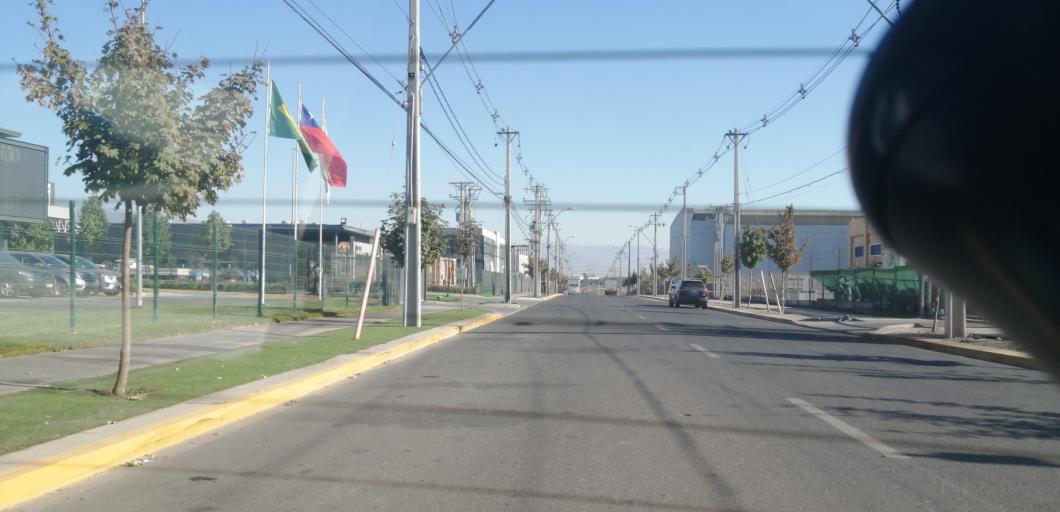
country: CL
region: Santiago Metropolitan
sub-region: Provincia de Santiago
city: Lo Prado
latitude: -33.4413
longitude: -70.7766
